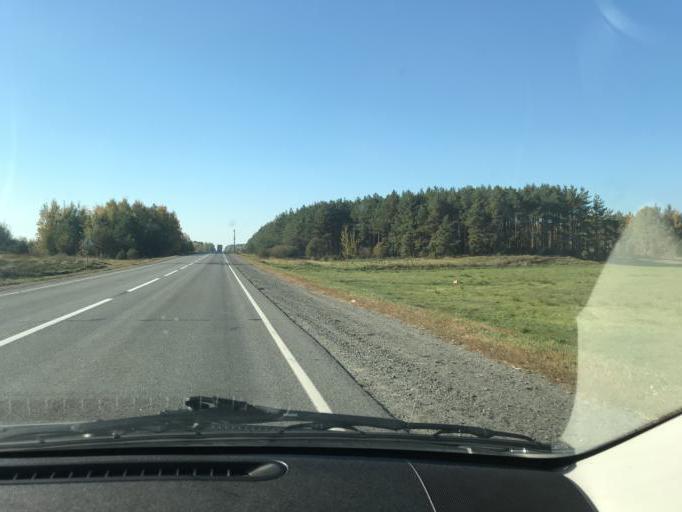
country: BY
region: Brest
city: Davyd-Haradok
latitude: 52.2444
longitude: 27.1483
